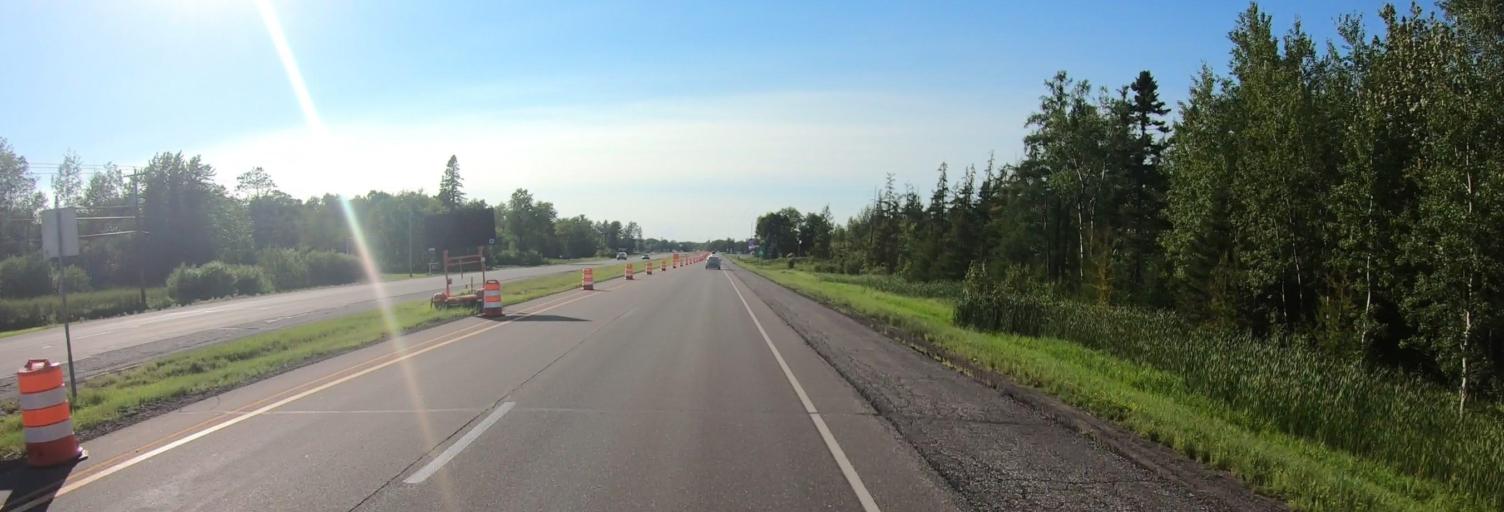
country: US
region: Minnesota
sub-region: Saint Louis County
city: Hermantown
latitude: 46.8483
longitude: -92.2731
